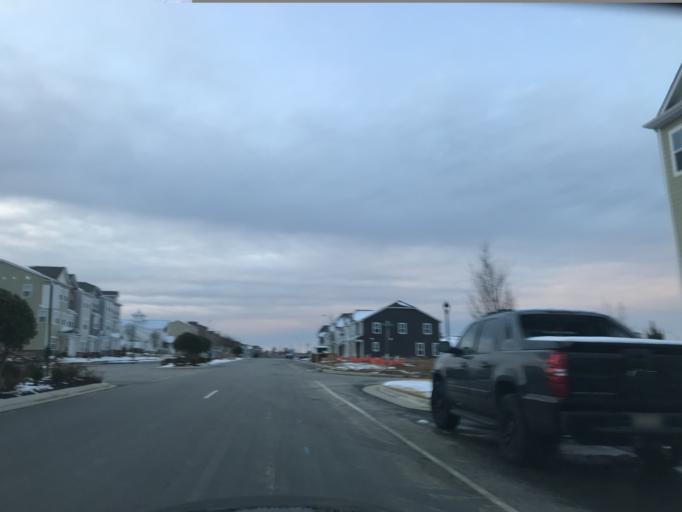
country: US
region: North Carolina
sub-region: Wake County
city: Knightdale
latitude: 35.8598
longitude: -78.5348
